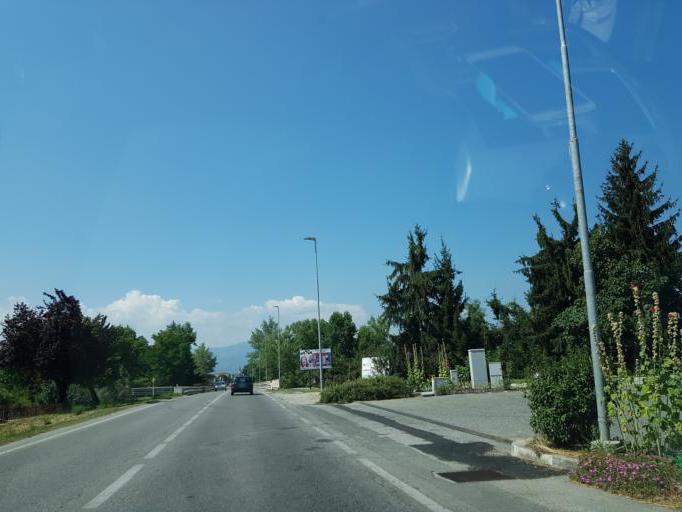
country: IT
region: Piedmont
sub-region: Provincia di Cuneo
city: Caraglio
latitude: 44.4085
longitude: 7.4420
